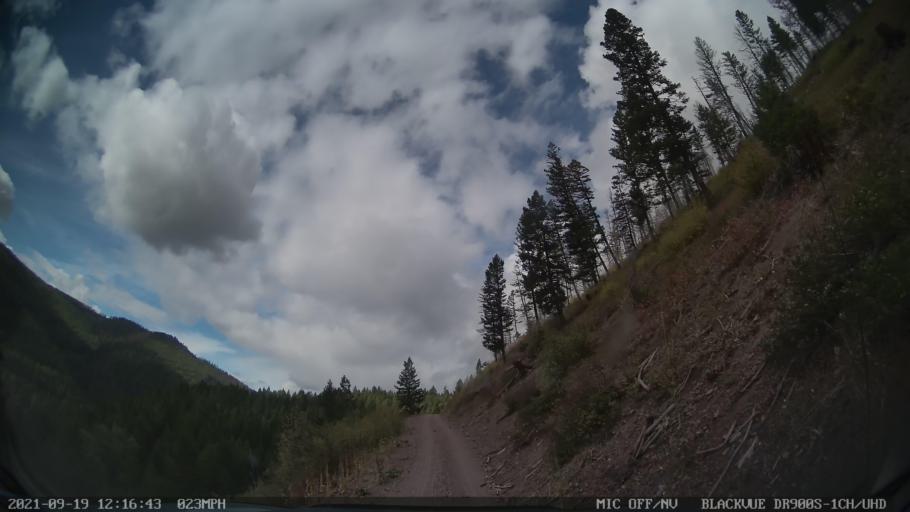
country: US
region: Montana
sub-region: Missoula County
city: Seeley Lake
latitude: 47.1701
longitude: -113.3535
